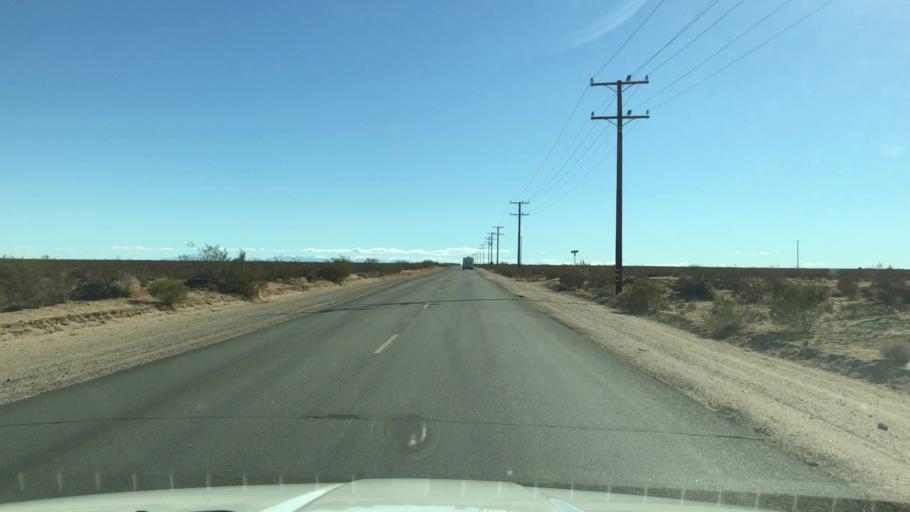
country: US
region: California
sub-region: Kern County
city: California City
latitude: 35.2359
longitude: -117.9859
